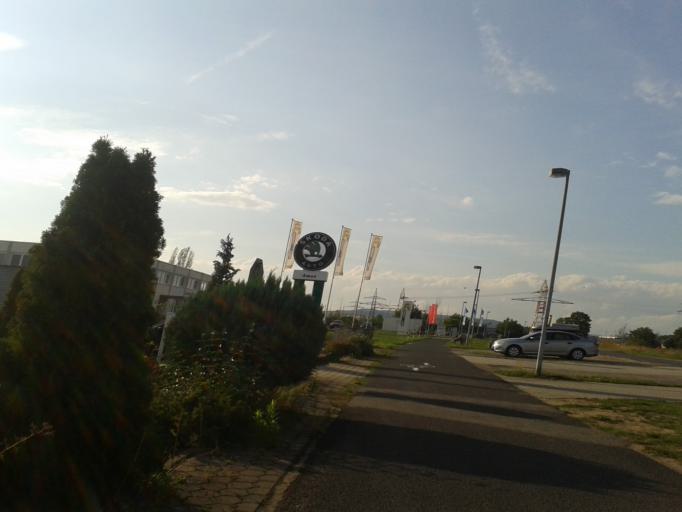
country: DE
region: Bavaria
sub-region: Upper Franconia
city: Bamberg
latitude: 49.9153
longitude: 10.9079
